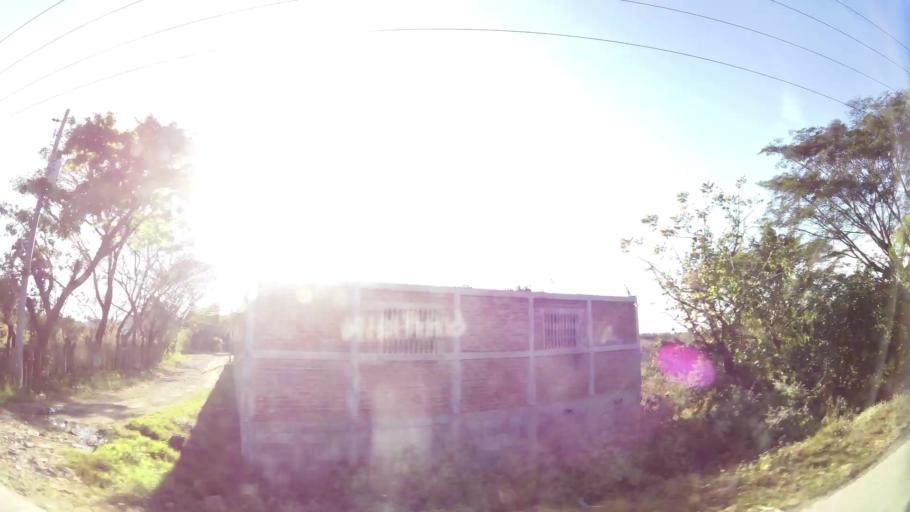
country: SV
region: Santa Ana
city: Metapan
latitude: 14.2910
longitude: -89.4626
